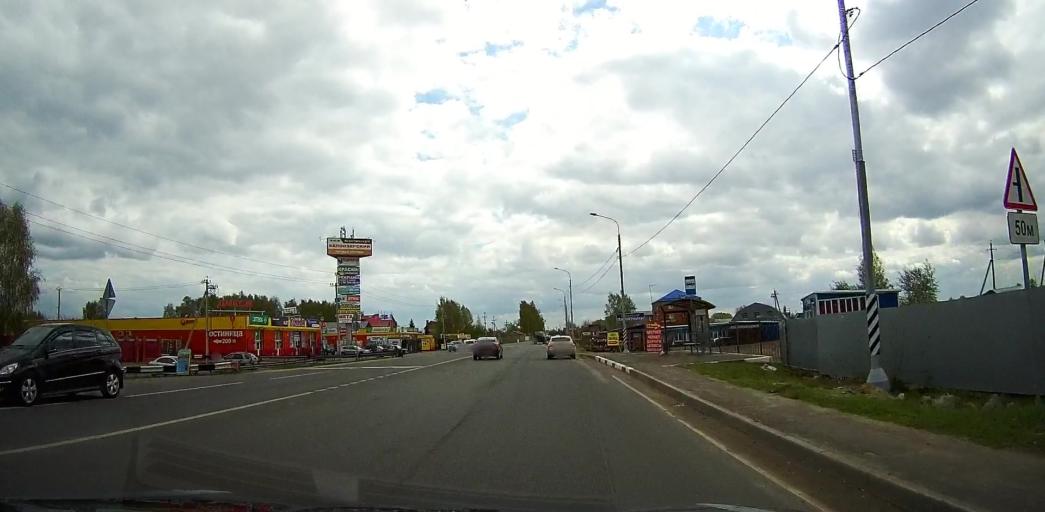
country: RU
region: Moskovskaya
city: Beloozerskiy
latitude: 55.4519
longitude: 38.4372
